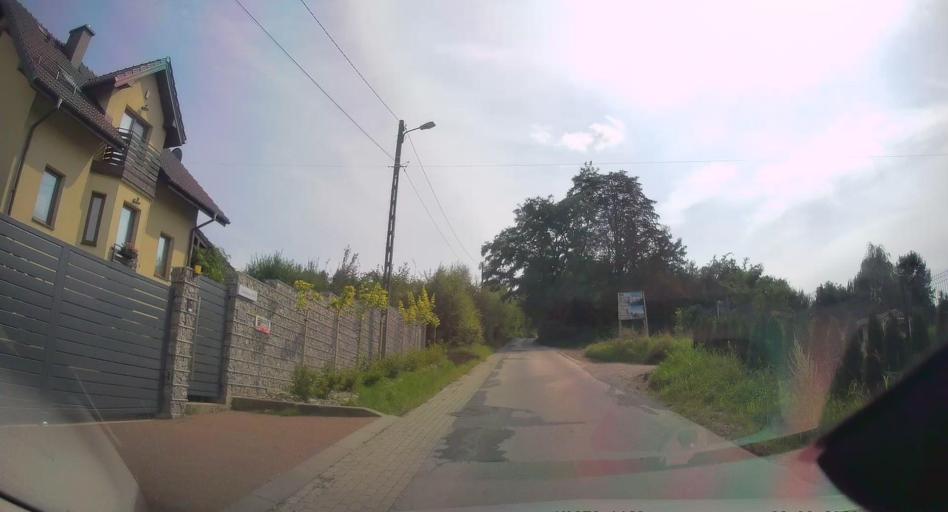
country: PL
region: Lesser Poland Voivodeship
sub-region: Powiat wielicki
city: Wieliczka
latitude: 49.9770
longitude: 20.0553
